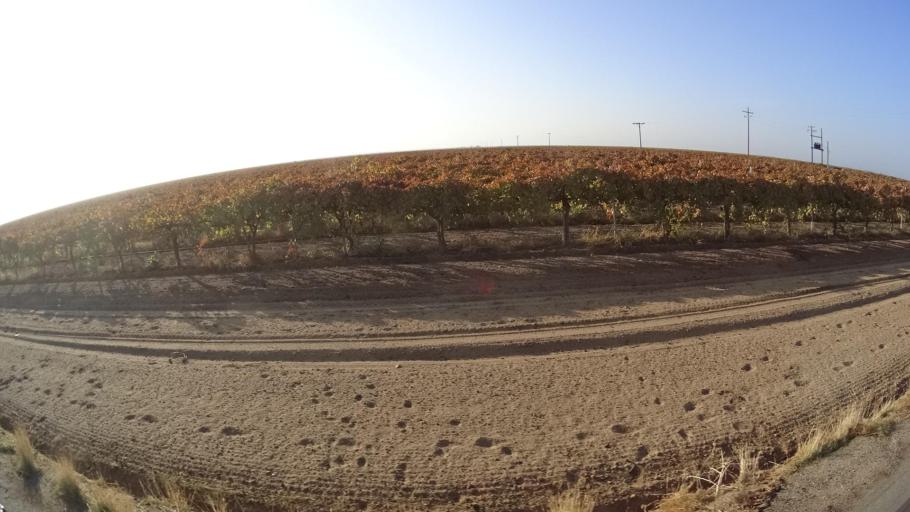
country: US
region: California
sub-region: Tulare County
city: Richgrove
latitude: 35.7762
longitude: -119.1156
